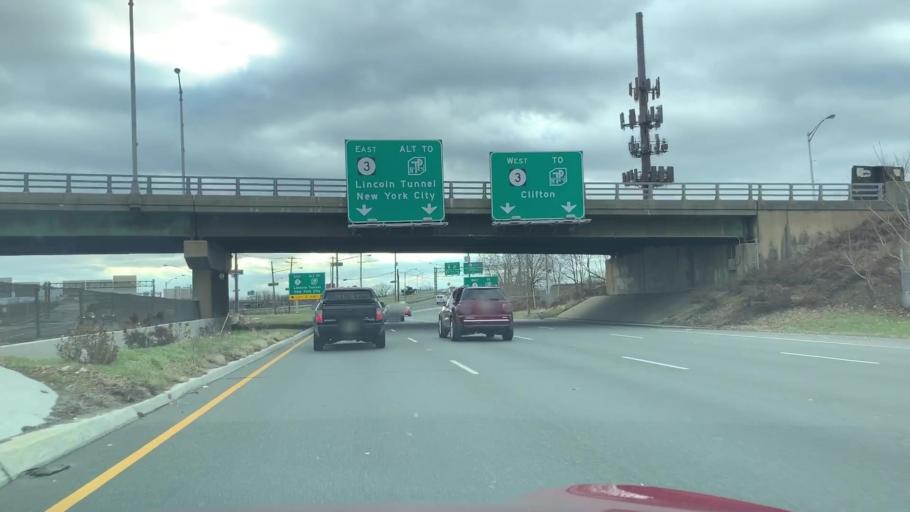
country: US
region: New Jersey
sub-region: Hudson County
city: Secaucus
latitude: 40.8084
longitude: -74.0727
